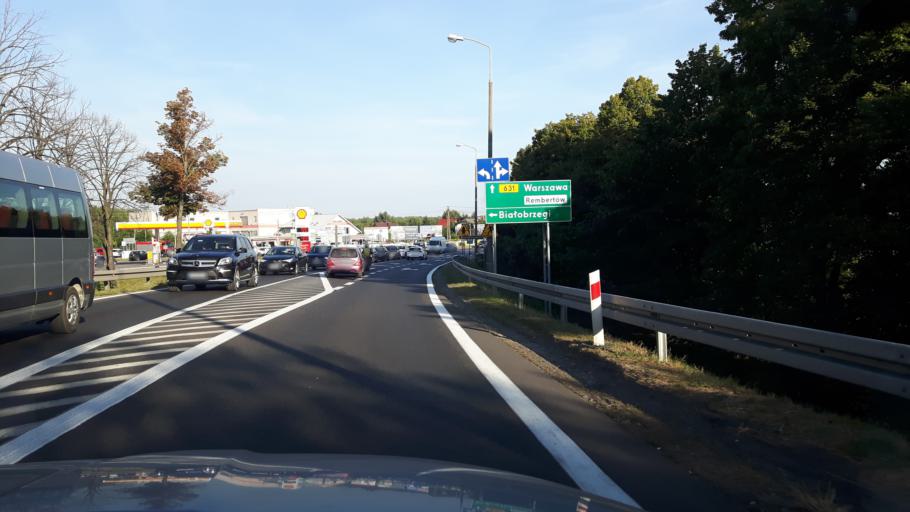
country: PL
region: Masovian Voivodeship
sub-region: Powiat legionowski
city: Nieporet
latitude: 52.4322
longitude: 21.0366
